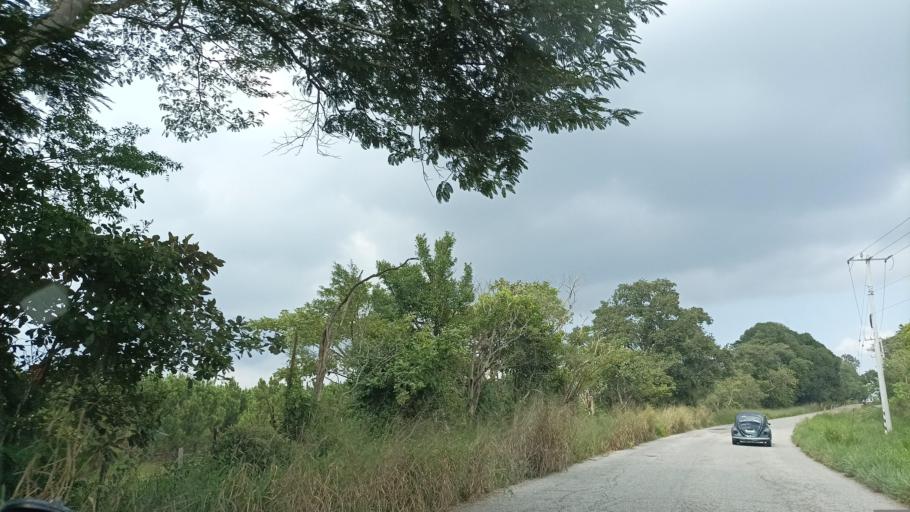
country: MX
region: Veracruz
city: Las Choapas
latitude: 17.8232
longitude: -94.1090
